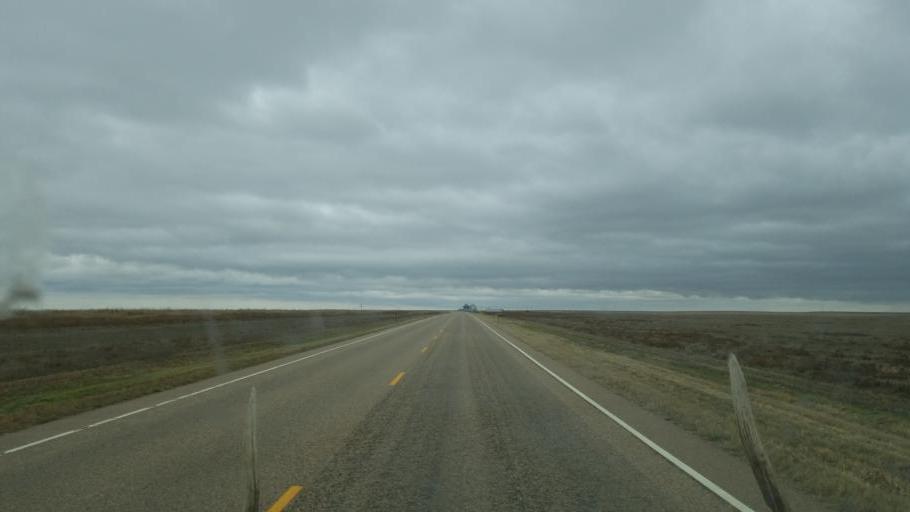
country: US
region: Colorado
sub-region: Cheyenne County
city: Cheyenne Wells
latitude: 38.8049
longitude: -102.6070
